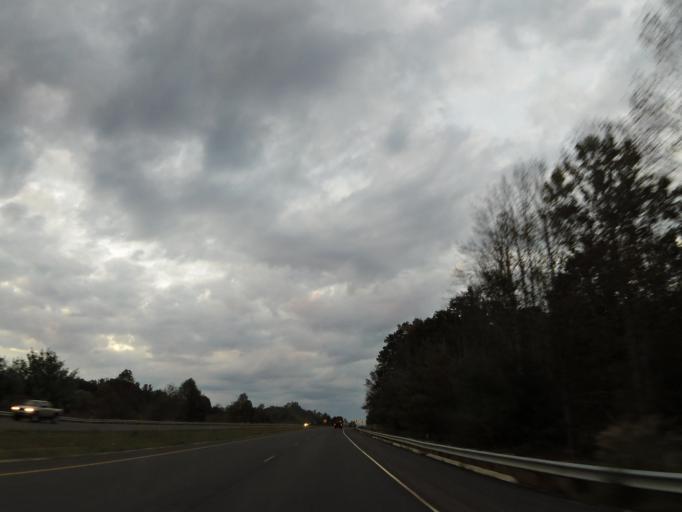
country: US
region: North Carolina
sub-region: Buncombe County
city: Weaverville
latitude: 35.7443
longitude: -82.6193
